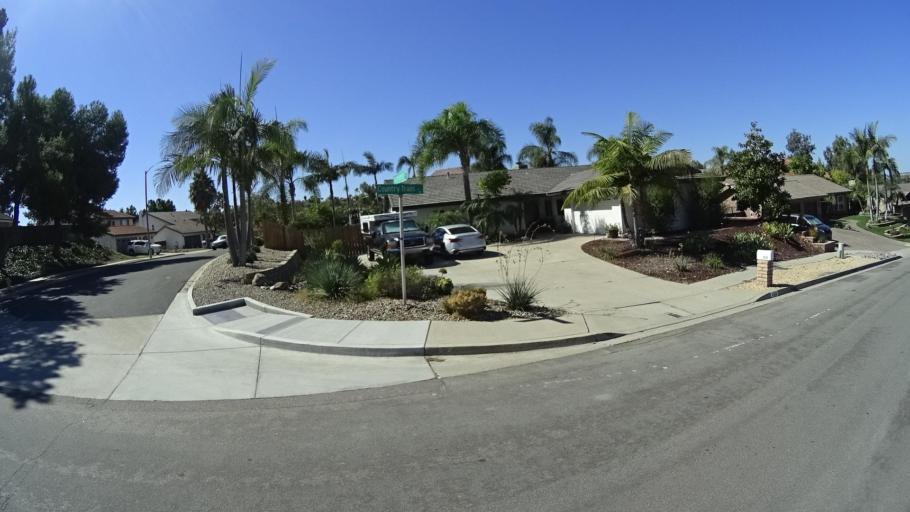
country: US
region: California
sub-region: San Diego County
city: Bonita
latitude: 32.6658
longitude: -116.9991
